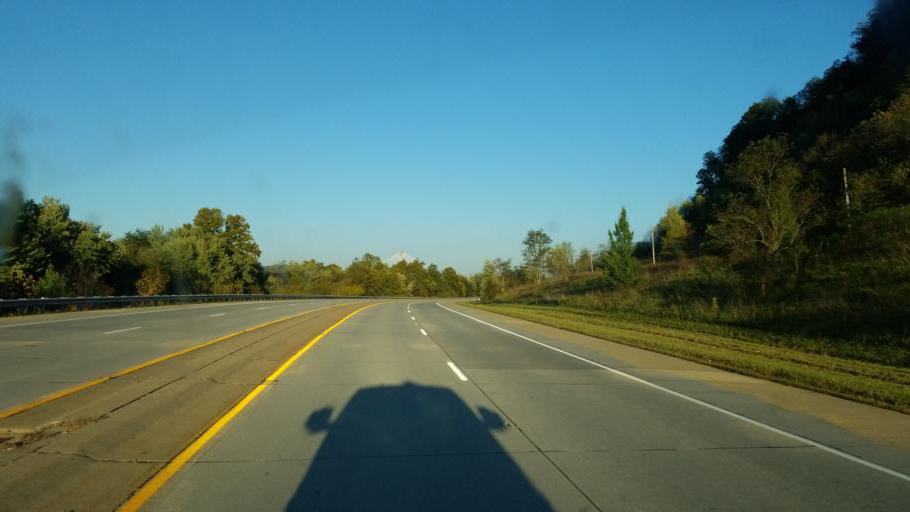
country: US
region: Ohio
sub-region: Scioto County
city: Portsmouth
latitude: 38.7253
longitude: -83.0106
